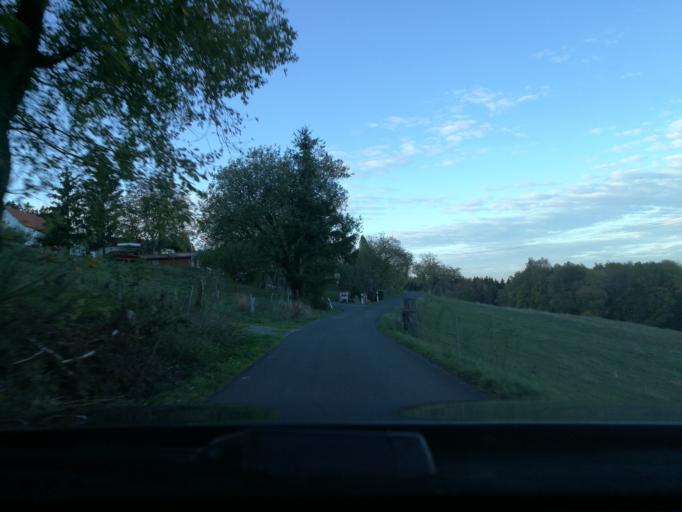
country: DE
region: Hesse
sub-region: Regierungsbezirk Kassel
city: Poppenhausen
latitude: 50.4741
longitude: 9.8580
